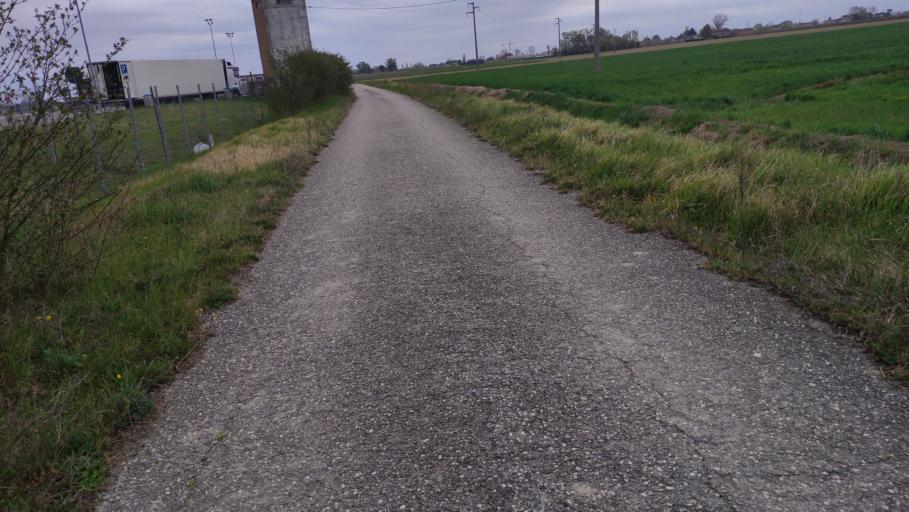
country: IT
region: Emilia-Romagna
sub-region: Provincia di Ravenna
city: Russi
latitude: 44.4018
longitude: 12.0443
